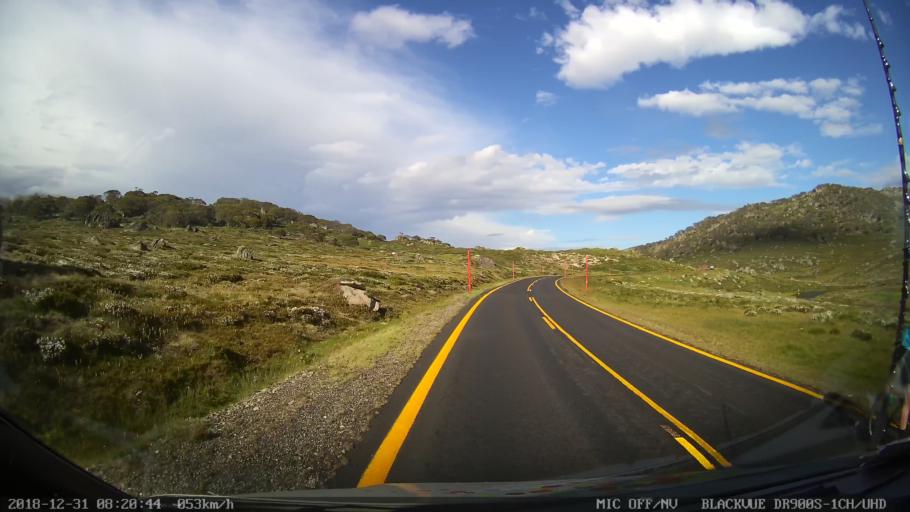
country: AU
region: New South Wales
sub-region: Snowy River
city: Jindabyne
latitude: -36.4259
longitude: 148.3733
